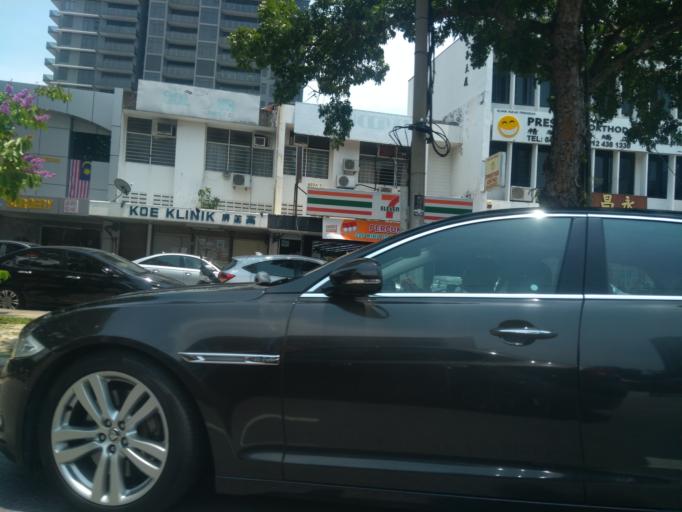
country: MY
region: Penang
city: George Town
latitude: 5.4302
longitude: 100.3129
